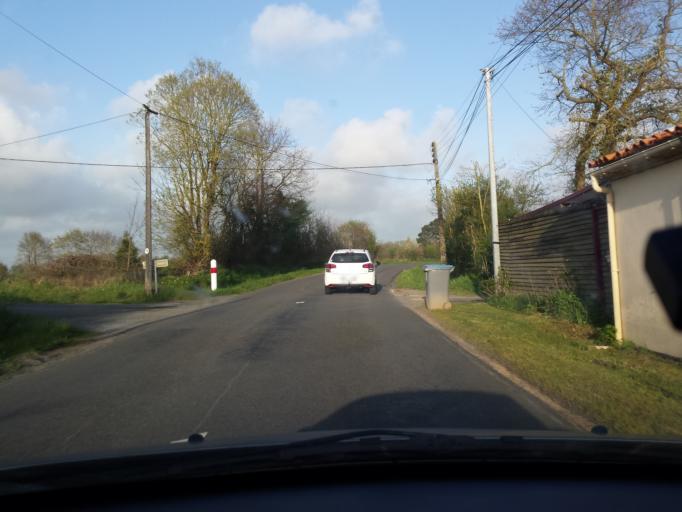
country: FR
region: Pays de la Loire
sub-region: Departement de la Vendee
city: Saint-Mathurin
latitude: 46.5650
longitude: -1.7228
